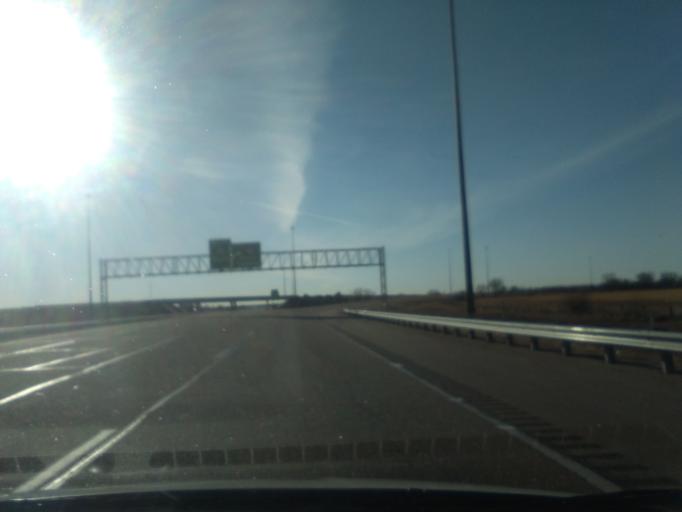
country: US
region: Colorado
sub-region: Sedgwick County
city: Julesburg
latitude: 41.0290
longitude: -102.1513
